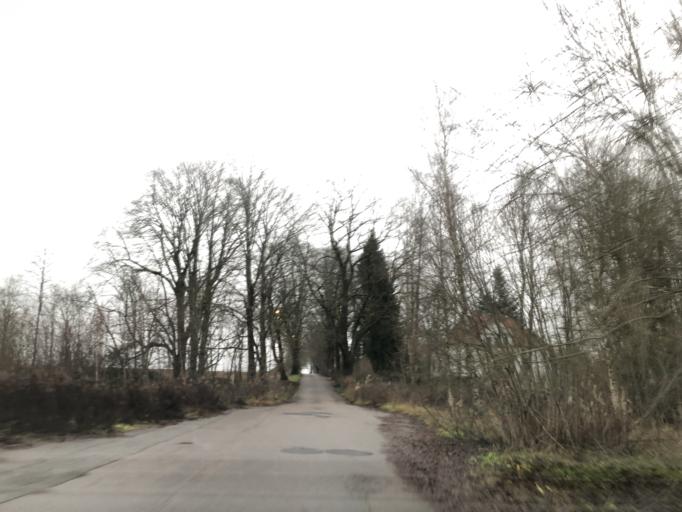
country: SE
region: Vaestra Goetaland
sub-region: Ulricehamns Kommun
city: Ulricehamn
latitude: 57.8417
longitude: 13.2910
